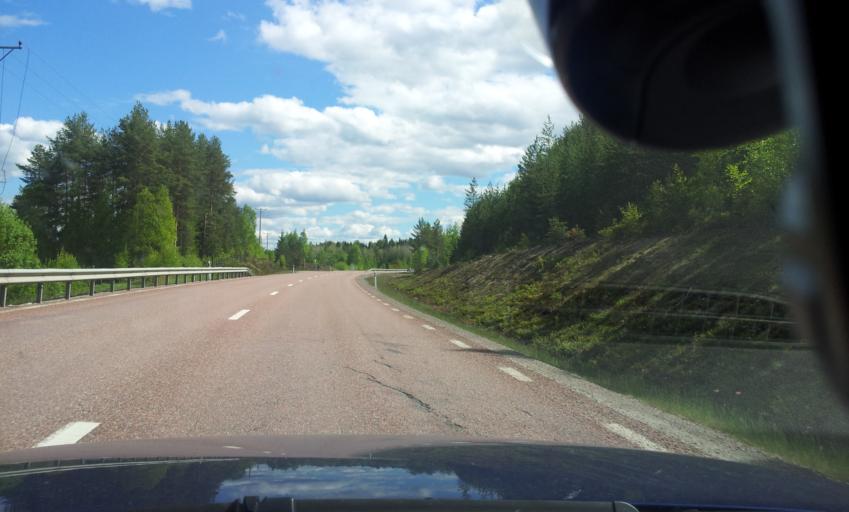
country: SE
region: Gaevleborg
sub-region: Ljusdals Kommun
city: Ljusdal
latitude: 61.8052
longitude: 16.1064
